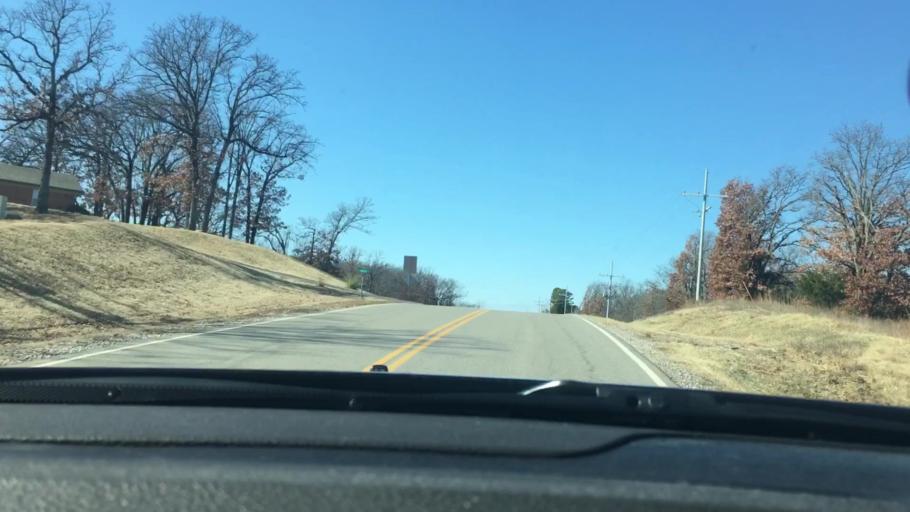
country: US
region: Oklahoma
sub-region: Murray County
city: Davis
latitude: 34.4772
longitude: -97.0469
